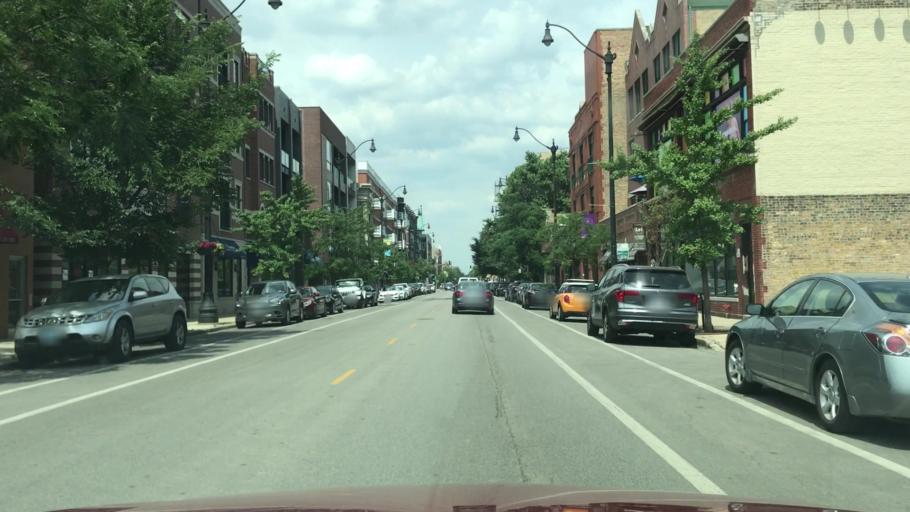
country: US
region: Illinois
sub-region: Cook County
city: Chicago
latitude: 41.9310
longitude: -87.6565
